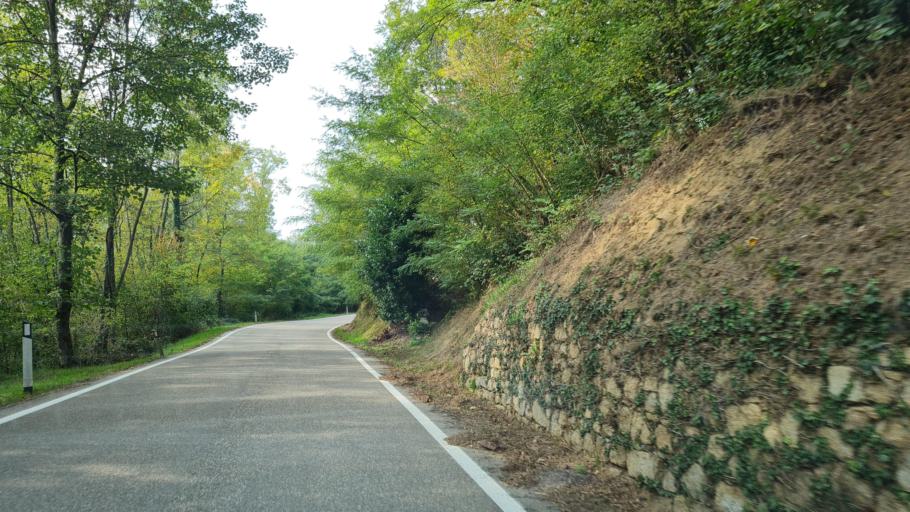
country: IT
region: Piedmont
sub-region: Provincia di Biella
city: Mezzana Mortigliengo
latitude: 45.6197
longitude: 8.1844
